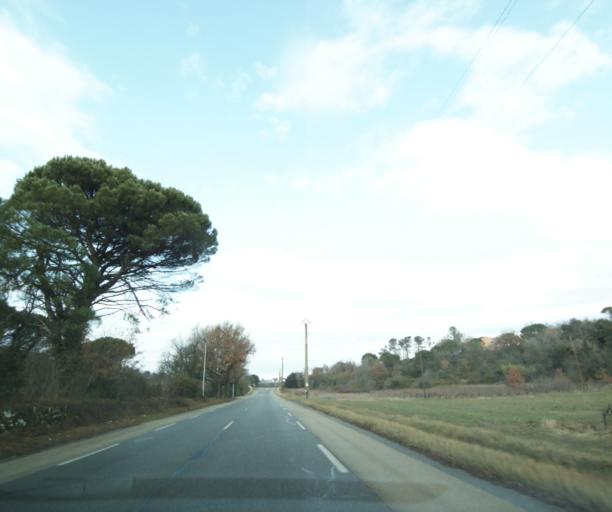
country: FR
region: Provence-Alpes-Cote d'Azur
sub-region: Departement du Var
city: Tourves
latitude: 43.4187
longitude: 5.9105
